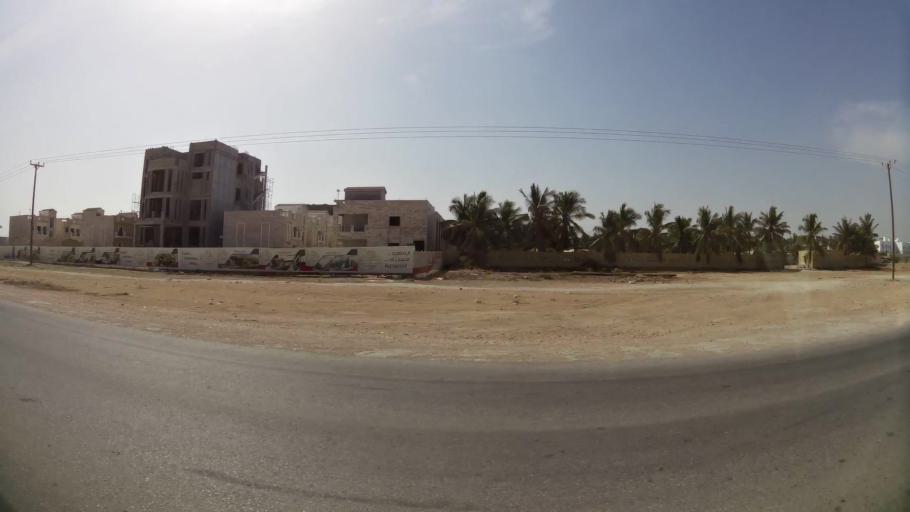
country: OM
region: Zufar
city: Salalah
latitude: 16.9923
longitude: 54.0199
